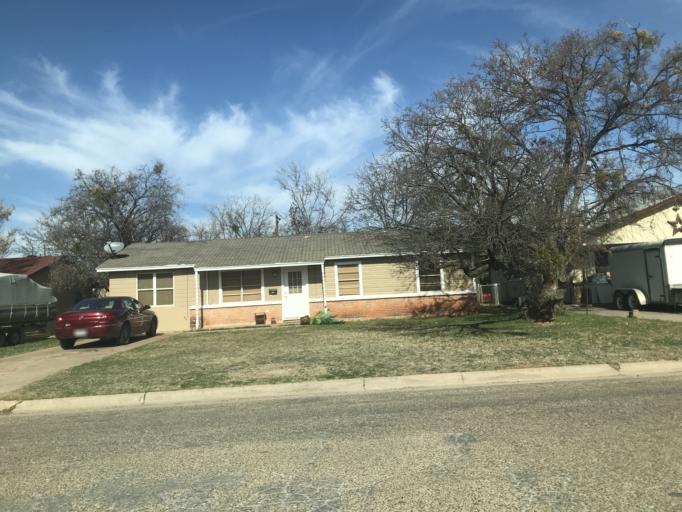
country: US
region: Texas
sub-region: Taylor County
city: Abilene
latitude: 32.4211
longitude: -99.7551
